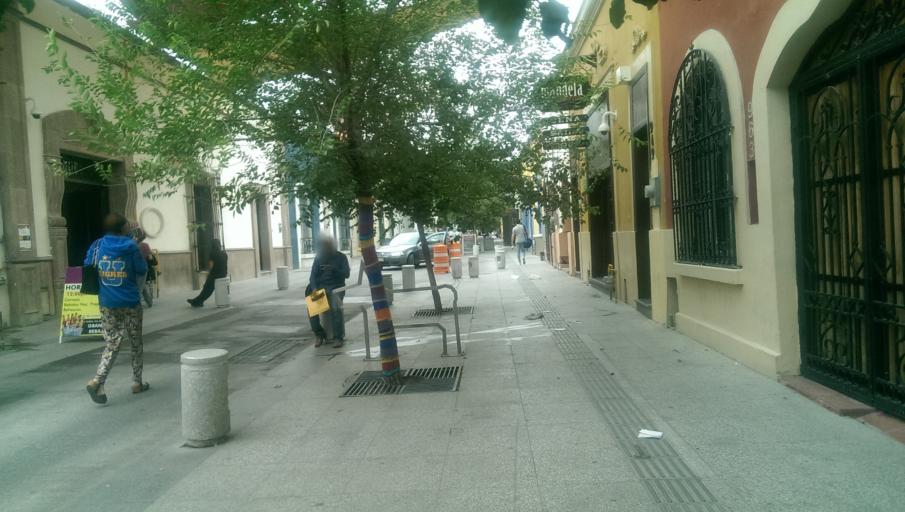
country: MX
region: Nuevo Leon
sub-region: Monterrey
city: Monterrey
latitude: 25.6664
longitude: -100.3068
